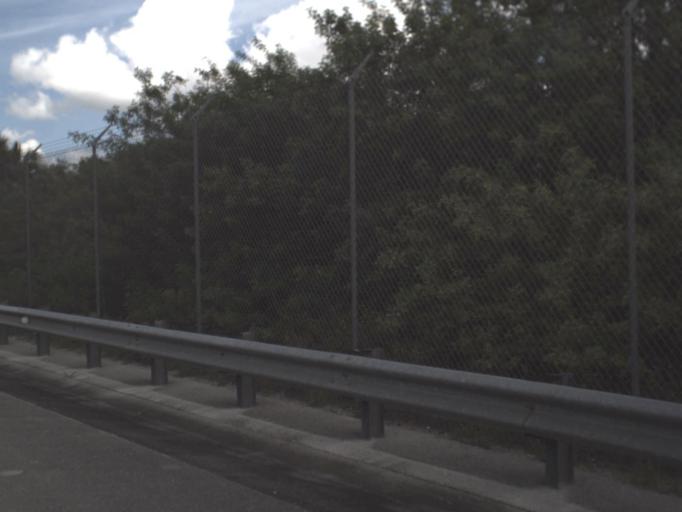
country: US
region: Florida
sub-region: Collier County
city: Lely Resort
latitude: 25.9799
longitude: -81.3495
